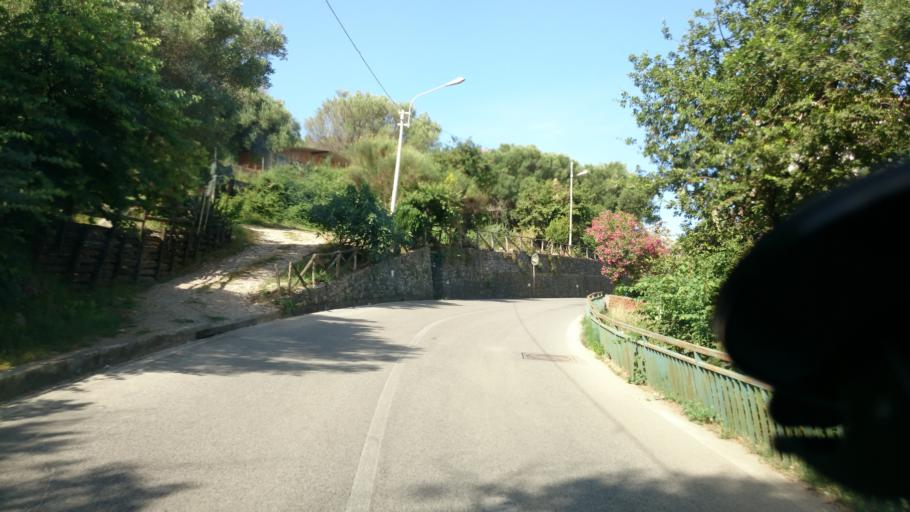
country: IT
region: Campania
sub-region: Provincia di Salerno
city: Sapri
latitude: 40.0675
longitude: 15.6330
